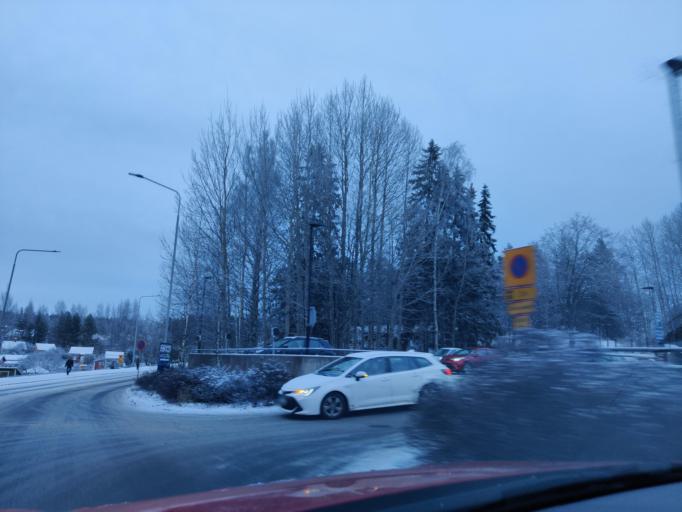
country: FI
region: Pirkanmaa
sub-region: Tampere
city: Tampere
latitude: 61.5021
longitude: 23.8014
